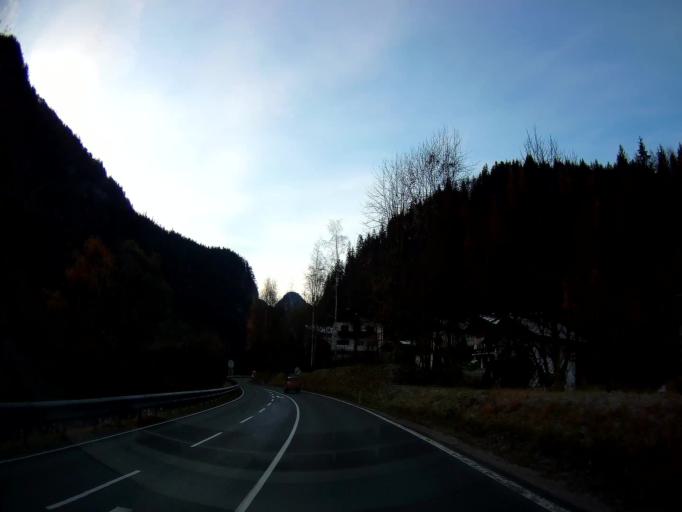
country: AT
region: Salzburg
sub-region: Politischer Bezirk Zell am See
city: Unken
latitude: 47.6450
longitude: 12.7277
